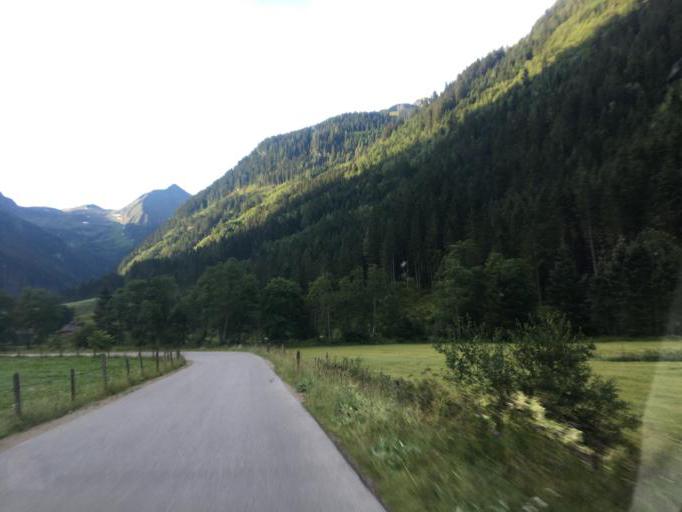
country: AT
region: Styria
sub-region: Politischer Bezirk Liezen
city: Haus
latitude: 47.3343
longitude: 13.7468
